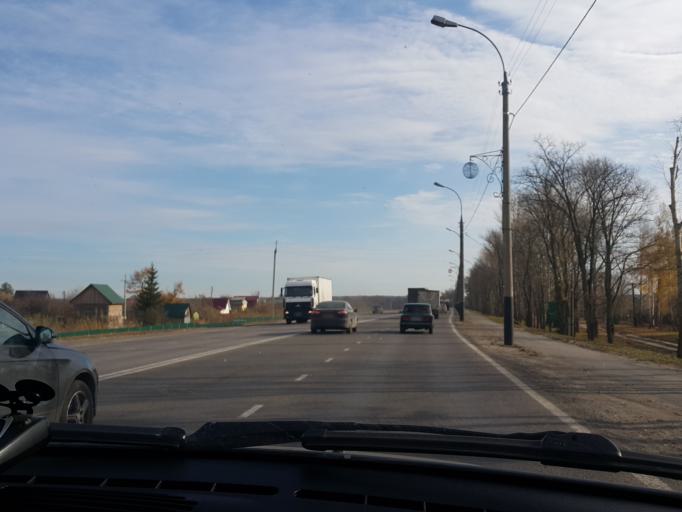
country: RU
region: Tambov
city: Tambov
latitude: 52.7217
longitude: 41.4859
